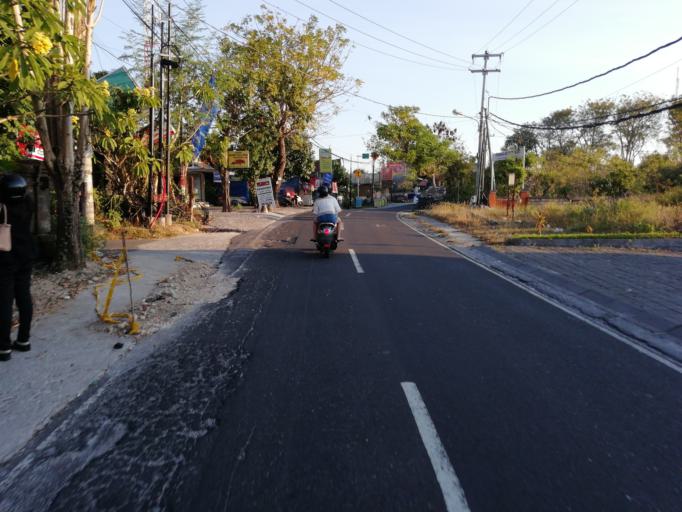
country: ID
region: Bali
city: Bualu
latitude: -8.8188
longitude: 115.1900
